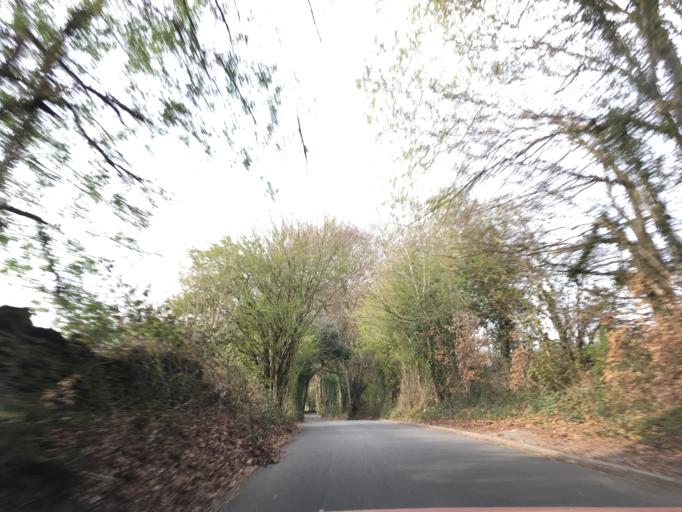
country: GB
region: Wales
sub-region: Caerphilly County Borough
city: Maesycwmmer
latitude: 51.6241
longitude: -3.2193
